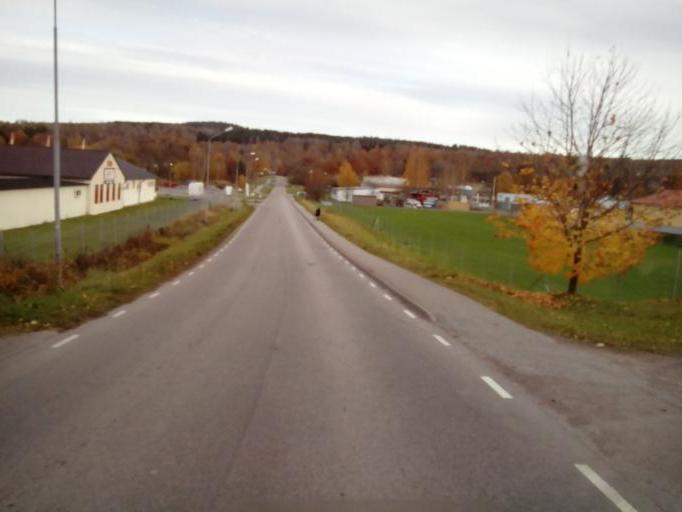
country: SE
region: OEstergoetland
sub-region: Kinda Kommun
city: Kisa
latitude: 57.9854
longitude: 15.6479
